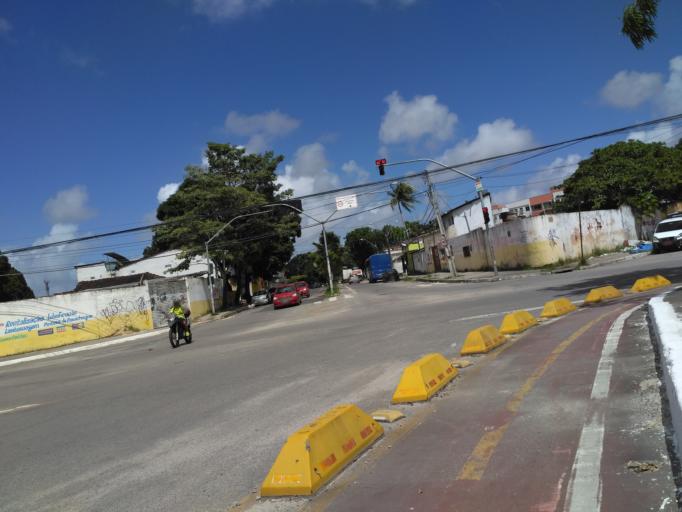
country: BR
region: Pernambuco
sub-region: Recife
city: Recife
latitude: -8.0470
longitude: -34.9361
